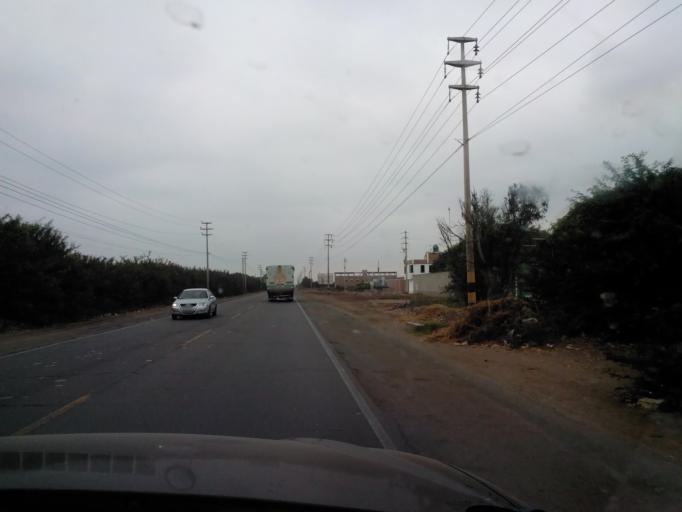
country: PE
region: Ica
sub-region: Provincia de Chincha
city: Chincha Baja
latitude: -13.4776
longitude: -76.1382
